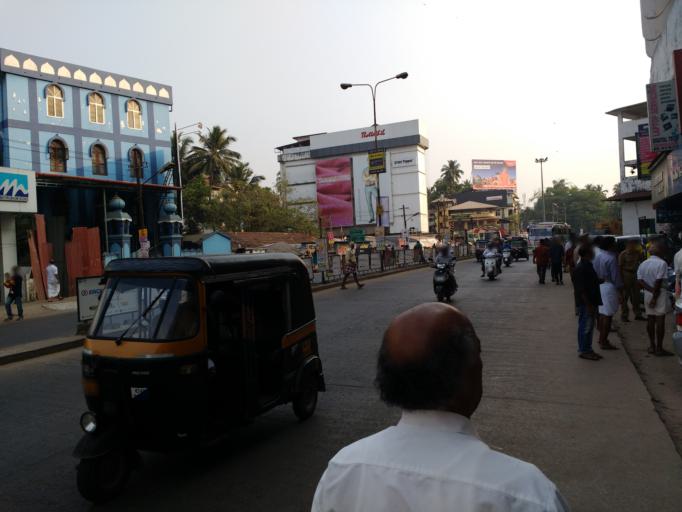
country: IN
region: Kerala
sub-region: Kozhikode
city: Kozhikode
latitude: 11.2564
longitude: 75.7865
